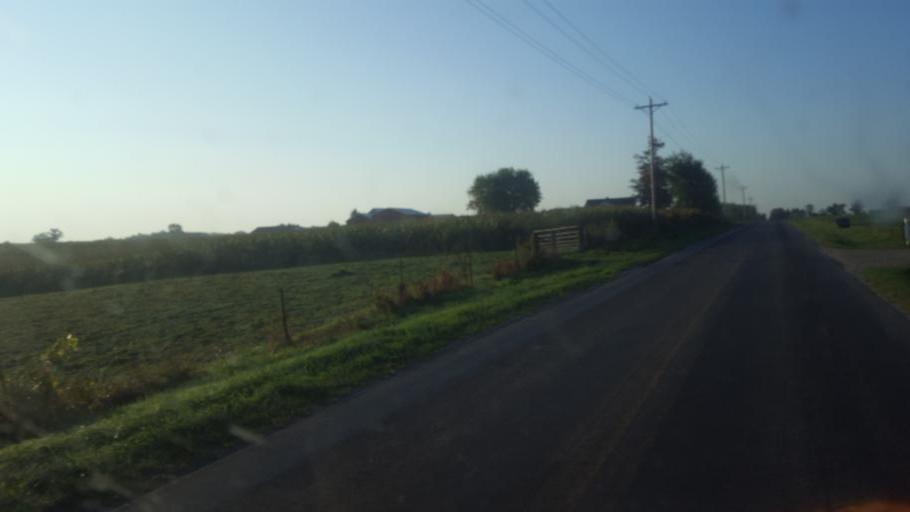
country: US
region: Indiana
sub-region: LaGrange County
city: Lagrange
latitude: 41.5898
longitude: -85.4241
